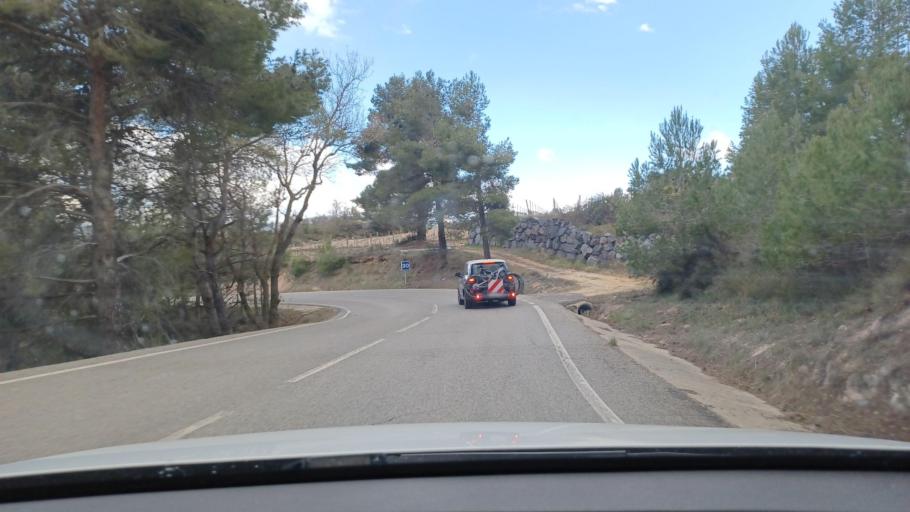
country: ES
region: Catalonia
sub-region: Provincia de Tarragona
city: la Morera de Montsant
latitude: 41.2676
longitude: 0.8768
